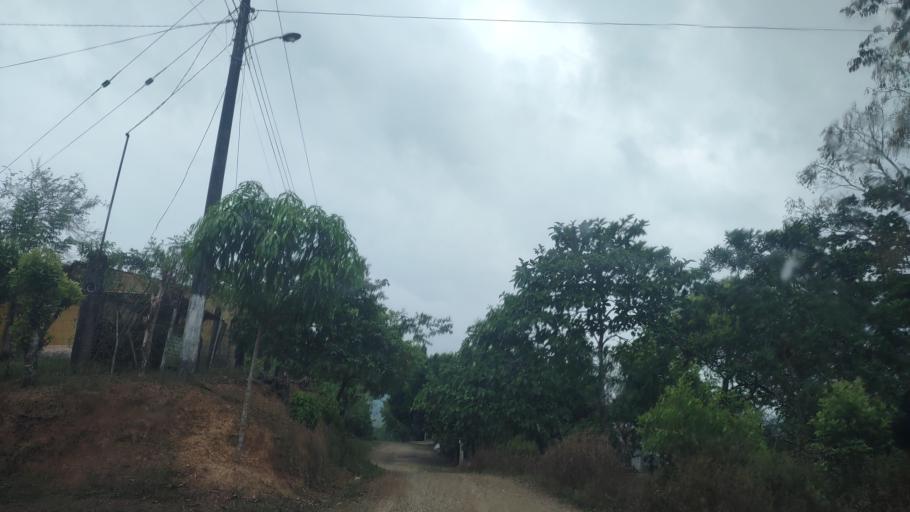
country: MX
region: Veracruz
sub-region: Uxpanapa
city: Poblado 10
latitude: 17.4479
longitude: -94.0983
